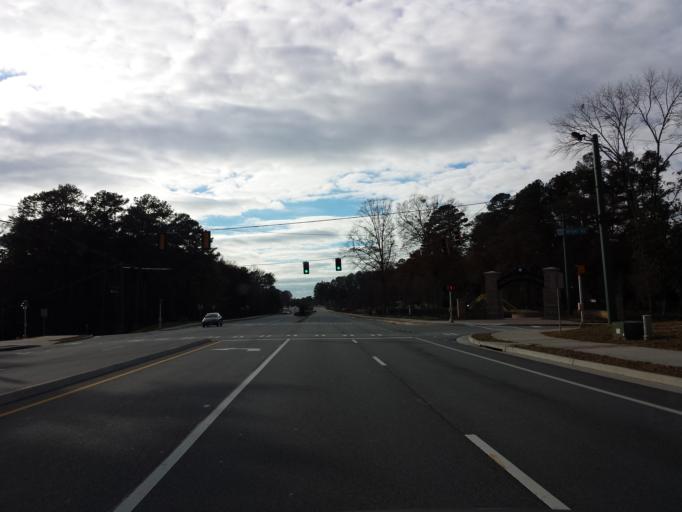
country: US
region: Georgia
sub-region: Fulton County
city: Sandy Springs
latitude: 33.9366
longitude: -84.3823
